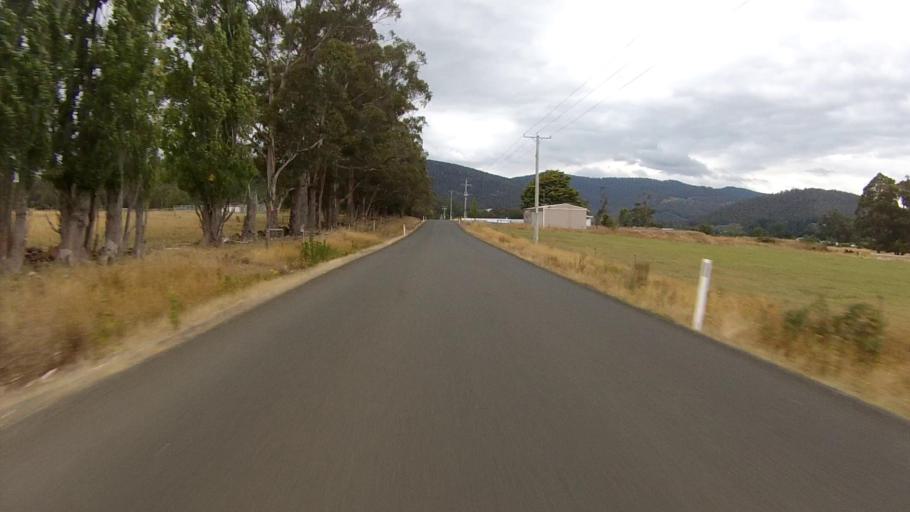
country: AU
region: Tasmania
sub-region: Huon Valley
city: Huonville
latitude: -42.9755
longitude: 147.0937
